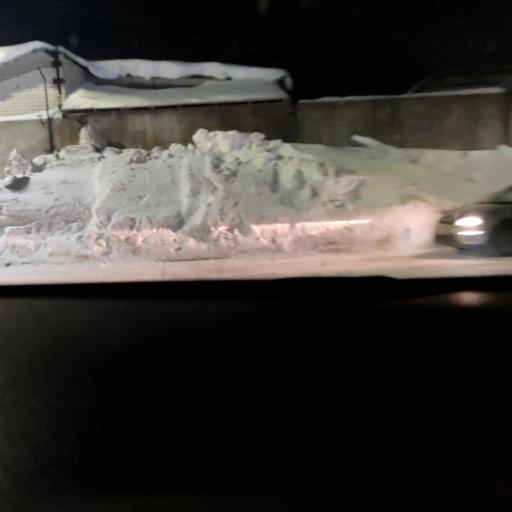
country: RU
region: Tatarstan
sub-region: Gorod Kazan'
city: Kazan
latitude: 55.7601
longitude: 49.2000
